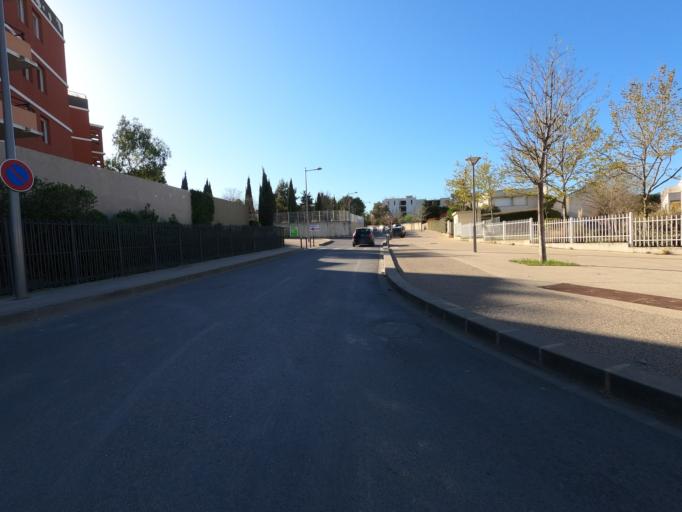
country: FR
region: Languedoc-Roussillon
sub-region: Departement de l'Herault
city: Montpellier
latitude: 43.5842
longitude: 3.8654
